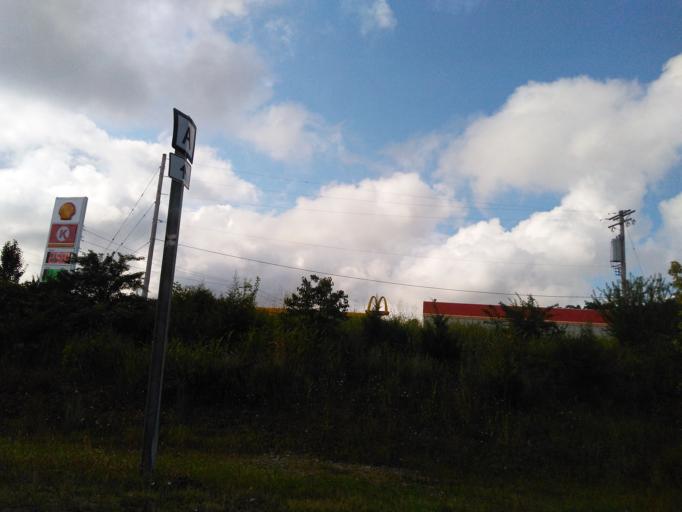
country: US
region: Missouri
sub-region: Jefferson County
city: Hillsboro
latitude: 38.2496
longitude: -90.5576
